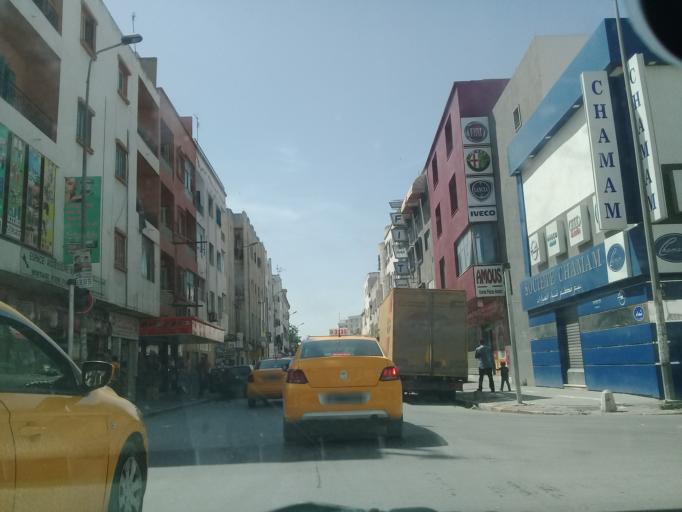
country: TN
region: Tunis
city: Tunis
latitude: 36.8117
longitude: 10.1760
